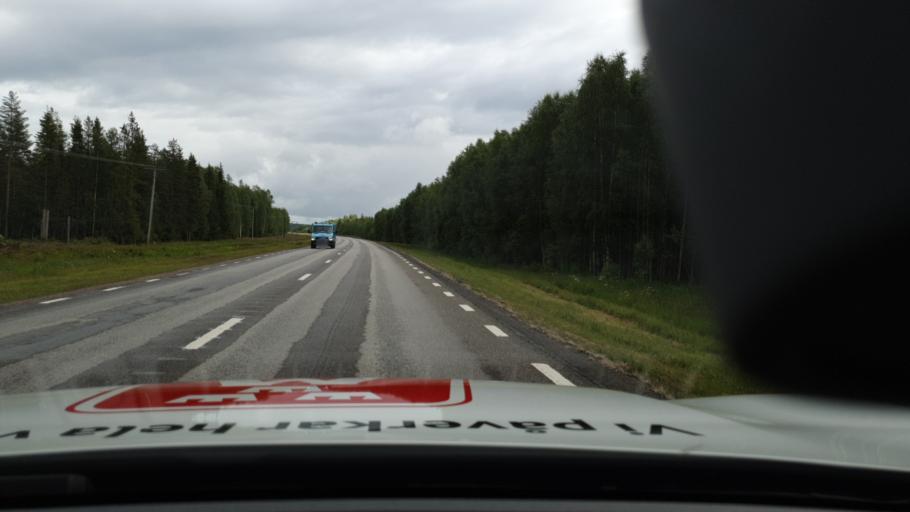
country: SE
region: Norrbotten
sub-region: Pitea Kommun
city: Rosvik
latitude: 65.5801
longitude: 21.6949
